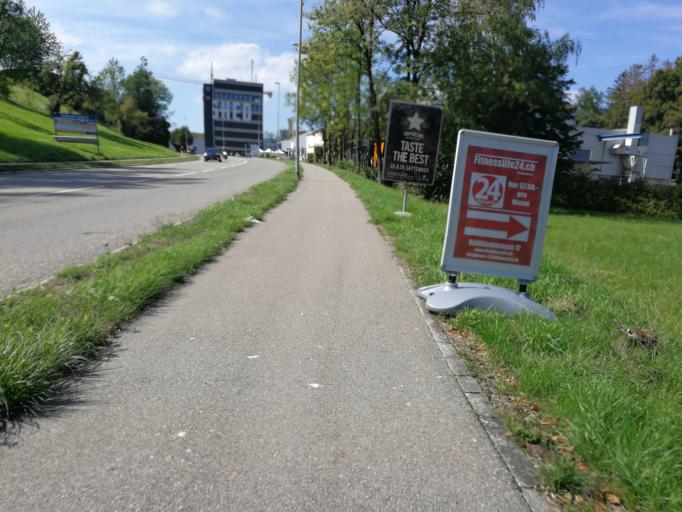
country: CH
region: Zurich
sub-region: Bezirk Horgen
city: Au
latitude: 47.2381
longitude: 8.6410
